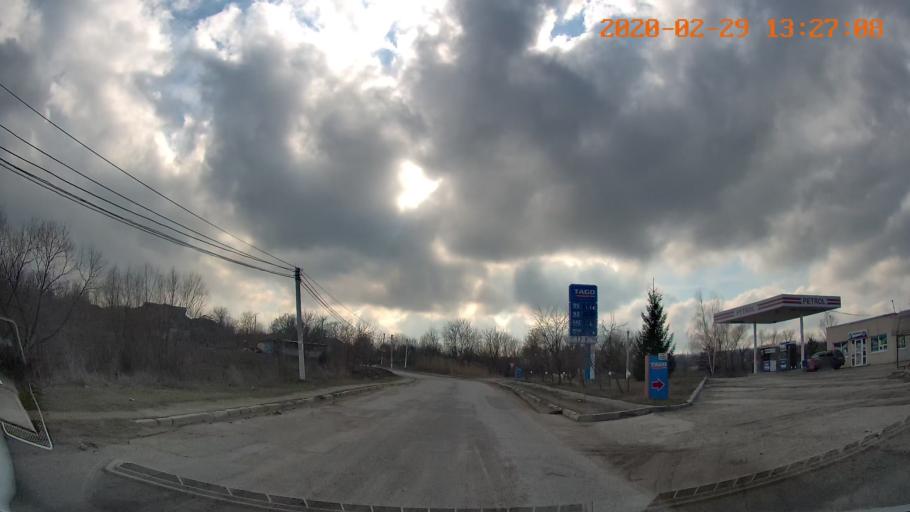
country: MD
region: Telenesti
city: Camenca
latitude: 47.9141
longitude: 28.6399
